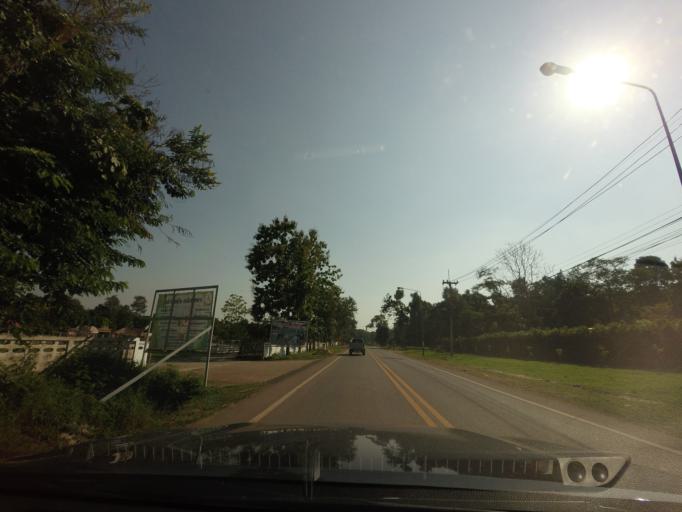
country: TH
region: Nan
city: Nan
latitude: 18.8017
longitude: 100.7995
